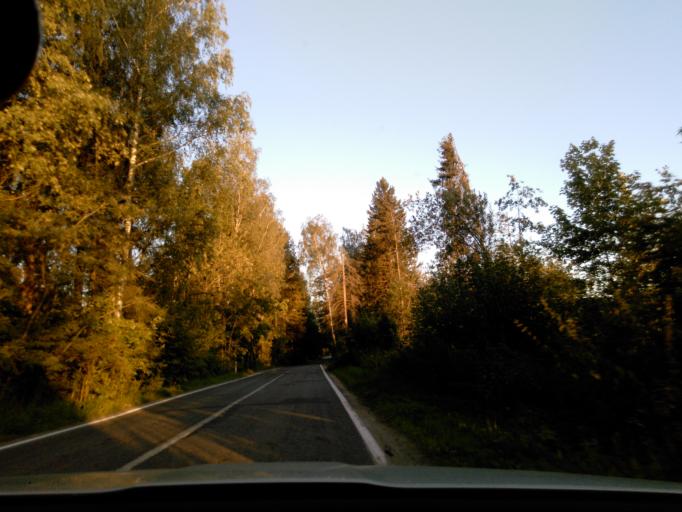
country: RU
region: Moskovskaya
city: Solnechnogorsk
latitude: 56.1304
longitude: 36.8811
